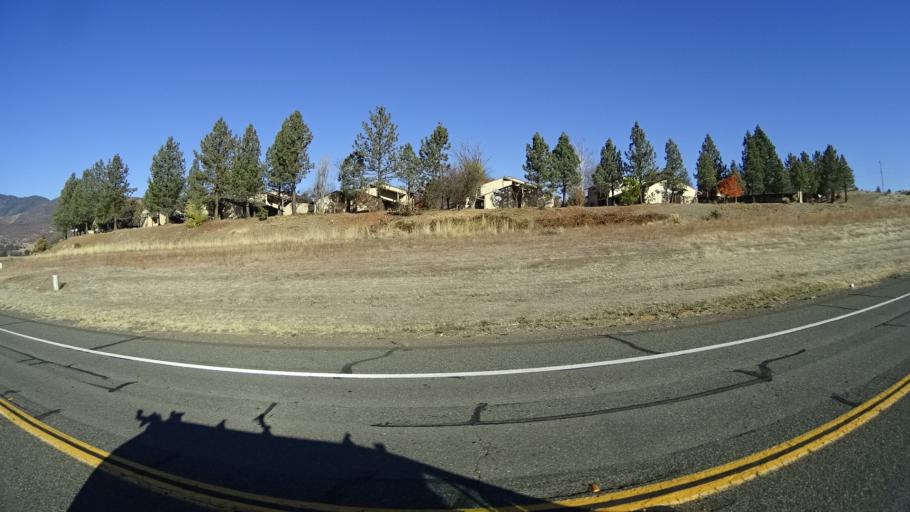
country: US
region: California
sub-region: Siskiyou County
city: Yreka
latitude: 41.7385
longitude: -122.6191
